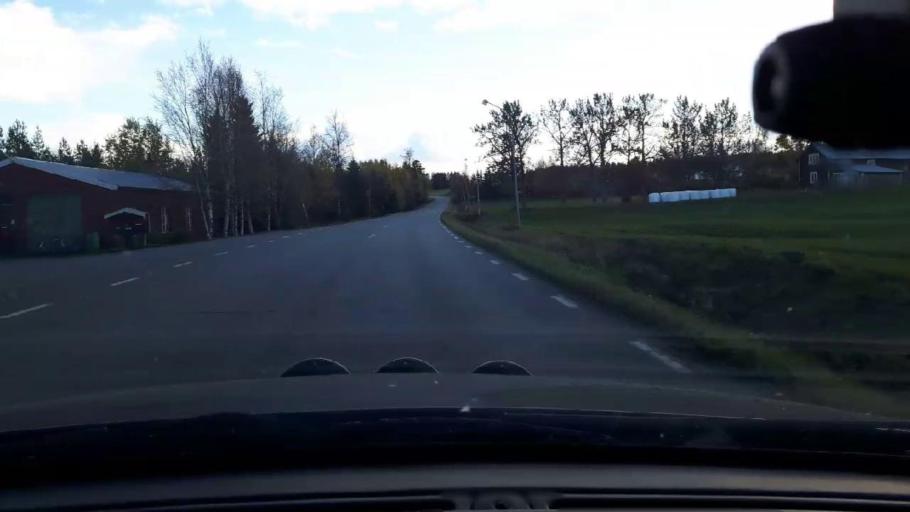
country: SE
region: Jaemtland
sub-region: Bergs Kommun
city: Hoverberg
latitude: 63.0254
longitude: 14.3445
